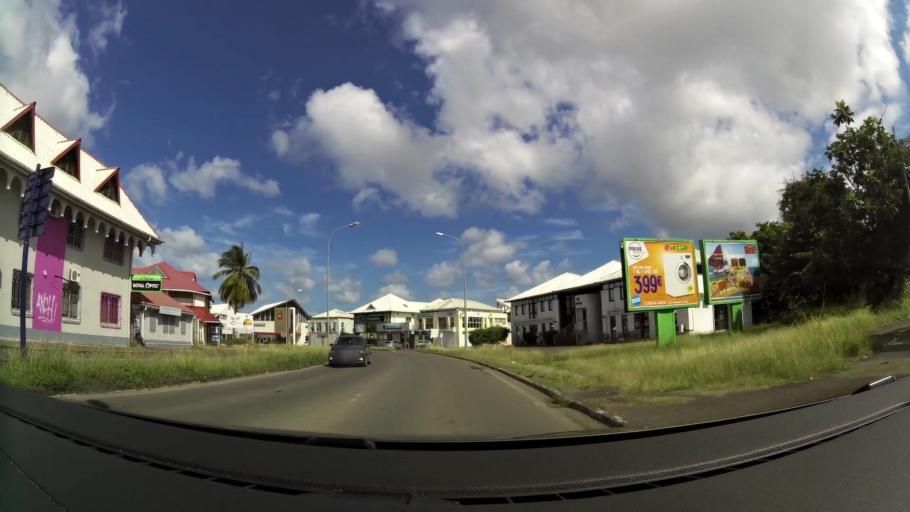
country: GP
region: Guadeloupe
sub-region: Guadeloupe
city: Pointe-a-Pitre
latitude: 16.2502
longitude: -61.5324
